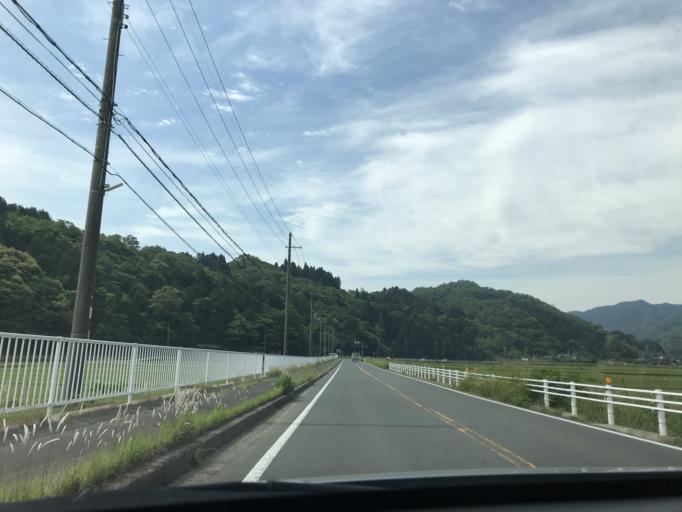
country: JP
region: Kyoto
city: Miyazu
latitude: 35.6653
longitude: 135.0236
